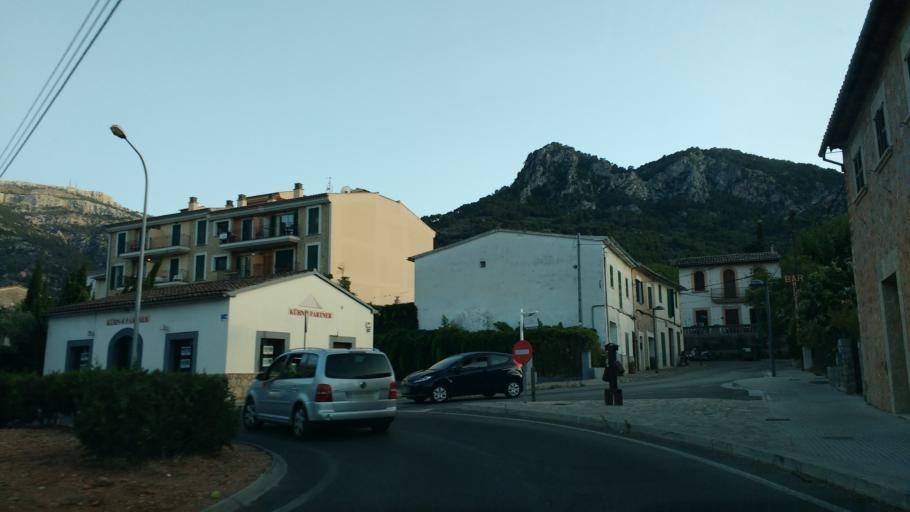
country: ES
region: Balearic Islands
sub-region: Illes Balears
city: Soller
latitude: 39.7711
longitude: 2.7061
